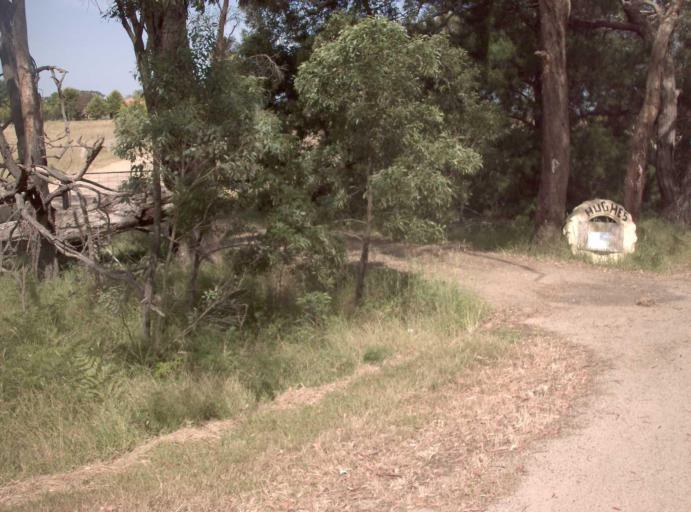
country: AU
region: Victoria
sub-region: Wellington
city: Sale
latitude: -38.2531
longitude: 147.1354
